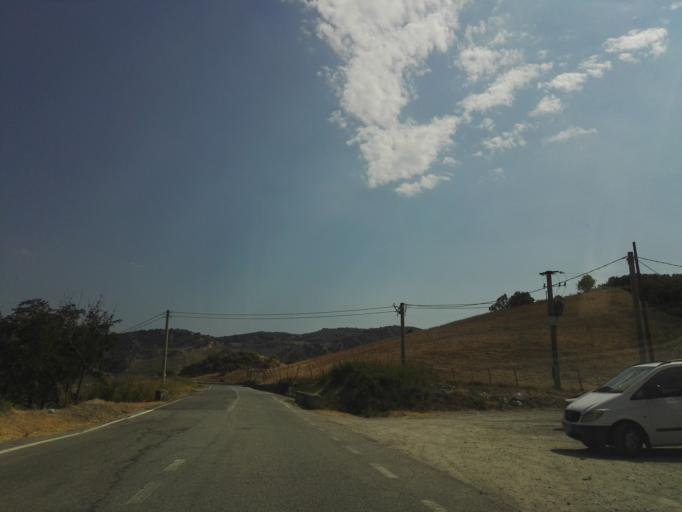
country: IT
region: Calabria
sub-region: Provincia di Reggio Calabria
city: Stilo
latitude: 38.4768
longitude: 16.4790
